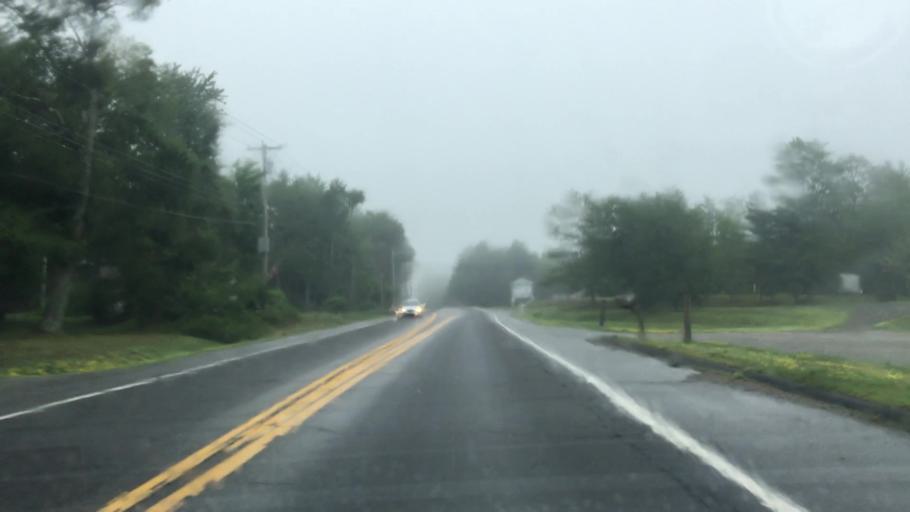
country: US
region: Maine
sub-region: Lincoln County
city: Wiscasset
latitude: 43.9811
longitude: -69.7024
